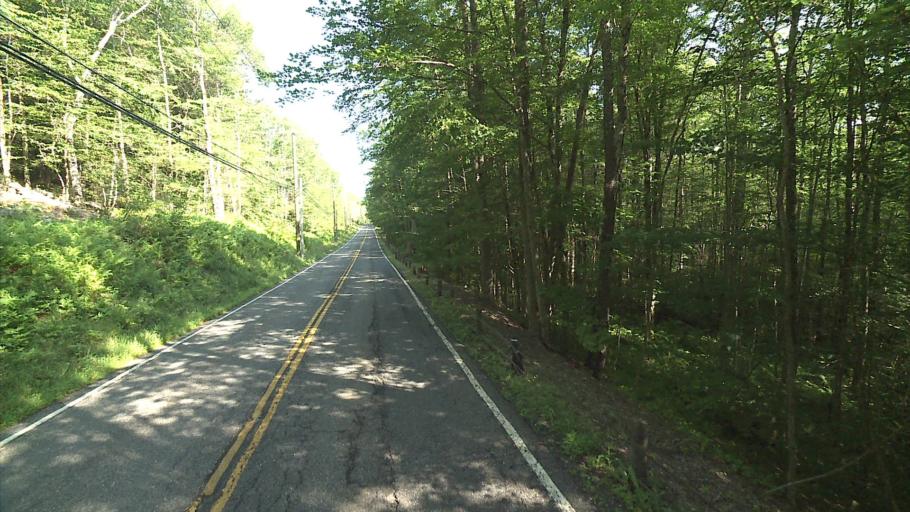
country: US
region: Connecticut
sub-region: Litchfield County
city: Winsted
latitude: 41.9973
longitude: -73.1007
